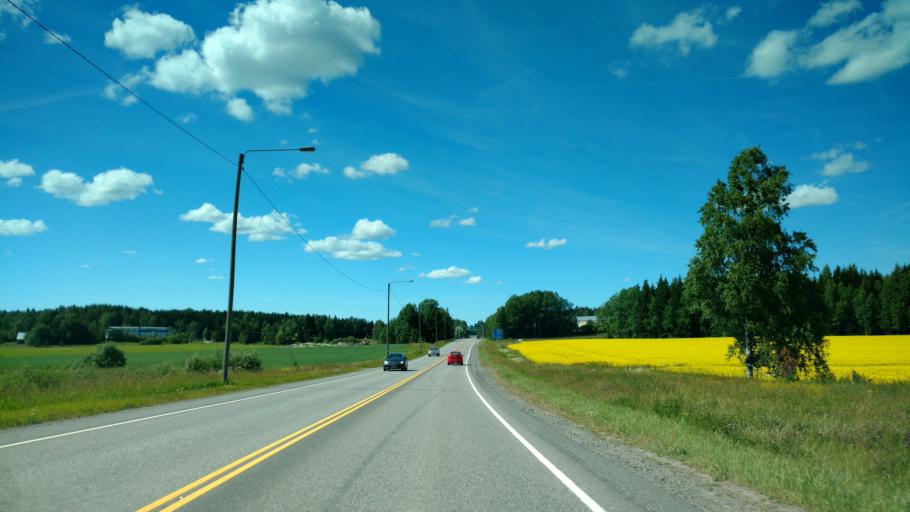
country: FI
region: Varsinais-Suomi
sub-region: Turku
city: Piikkioe
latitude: 60.4479
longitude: 22.4675
